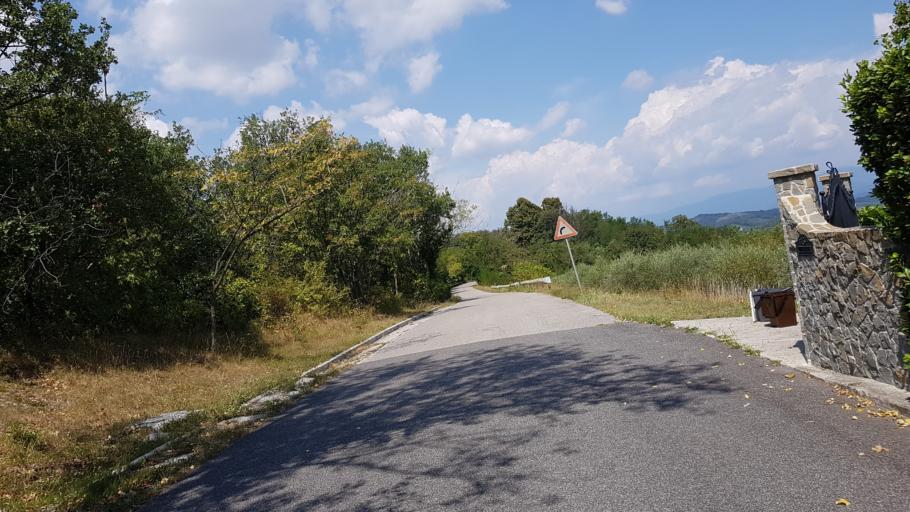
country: IT
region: Friuli Venezia Giulia
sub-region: Provincia di Gorizia
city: Cormons
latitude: 45.9679
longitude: 13.4703
